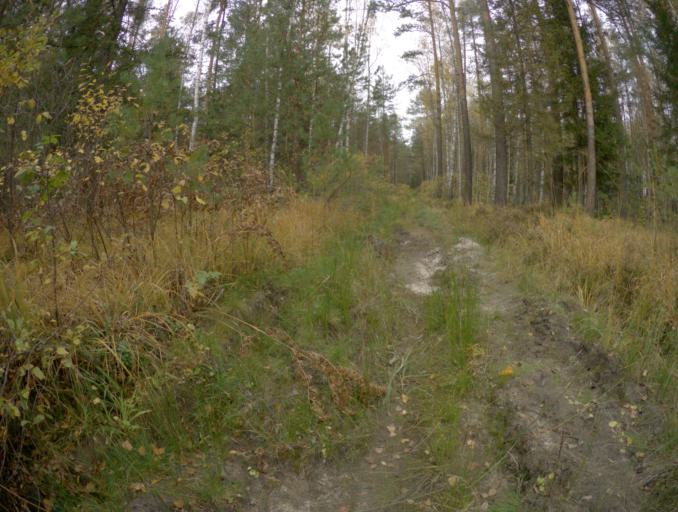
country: RU
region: Vladimir
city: Raduzhnyy
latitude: 55.9371
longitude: 40.3354
